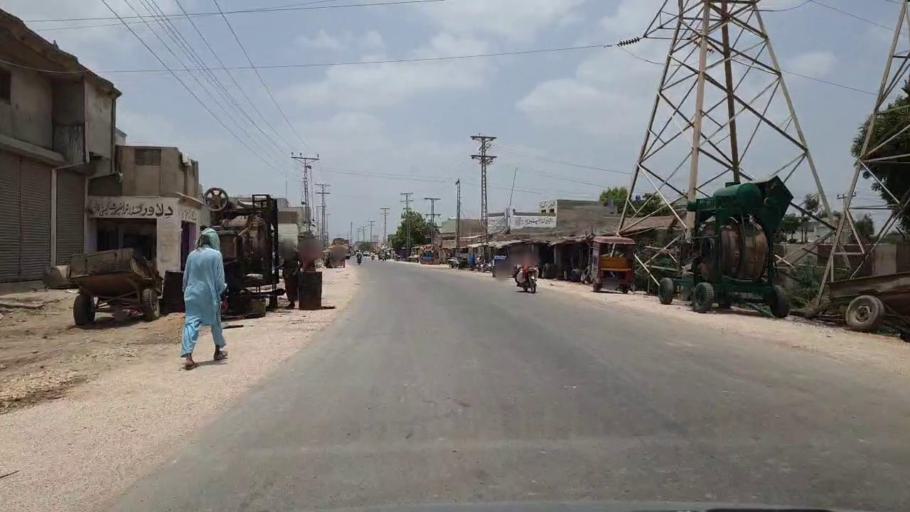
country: PK
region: Sindh
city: Naukot
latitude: 24.8522
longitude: 69.4081
